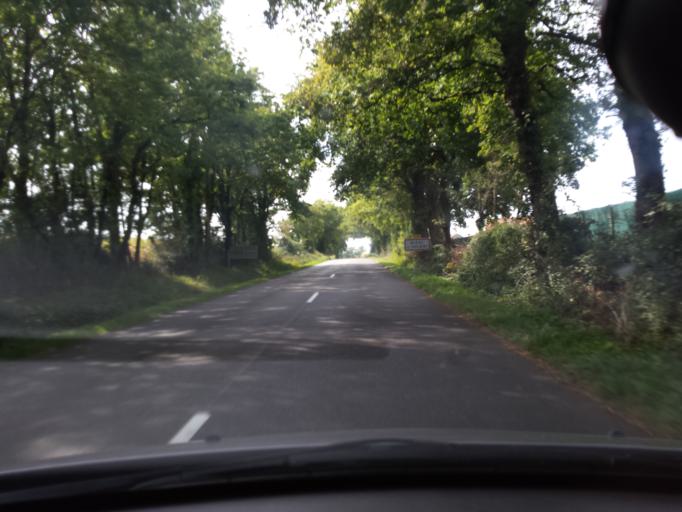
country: FR
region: Pays de la Loire
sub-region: Departement de la Vendee
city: Nieul-le-Dolent
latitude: 46.5774
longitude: -1.4966
